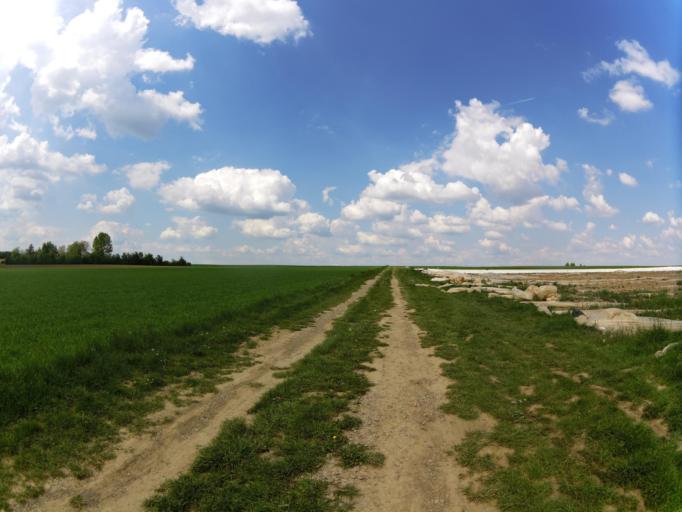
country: DE
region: Bavaria
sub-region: Regierungsbezirk Unterfranken
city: Sulzdorf
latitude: 49.6326
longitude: 9.9109
